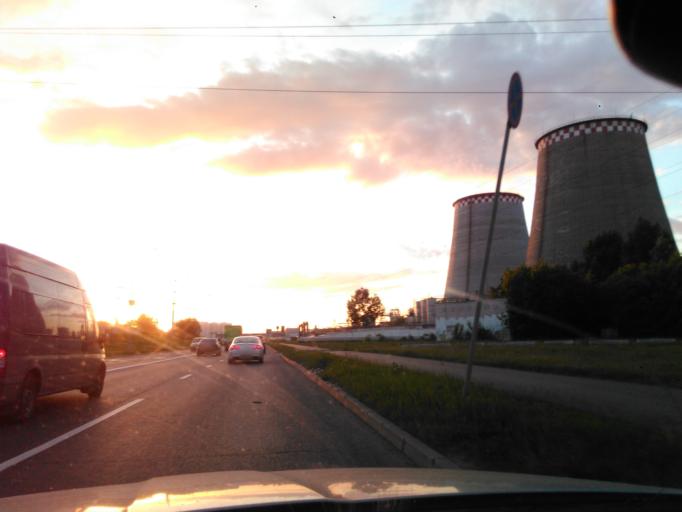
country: RU
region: Moscow
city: Businovo
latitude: 55.8864
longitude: 37.5059
